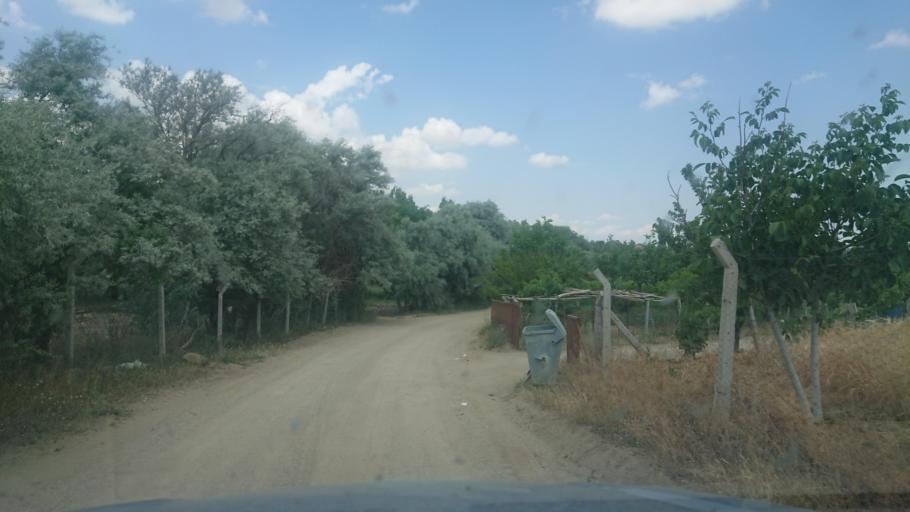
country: TR
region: Aksaray
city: Agacoren
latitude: 38.9324
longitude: 33.9552
